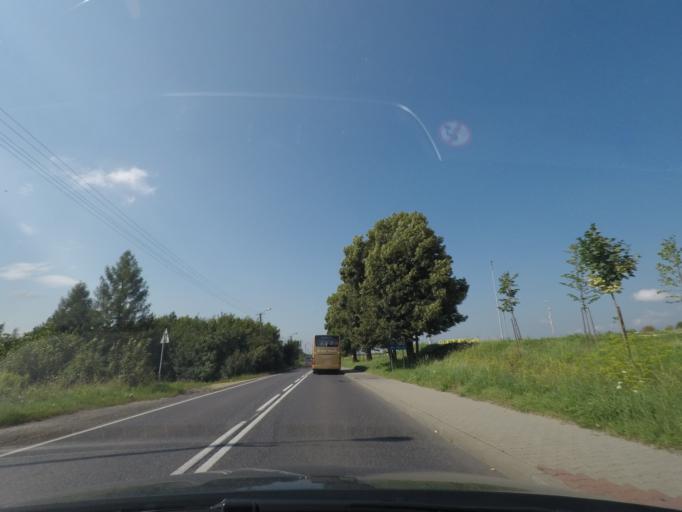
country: PL
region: Lesser Poland Voivodeship
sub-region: Powiat chrzanowski
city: Libiaz
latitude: 50.0956
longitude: 19.3016
